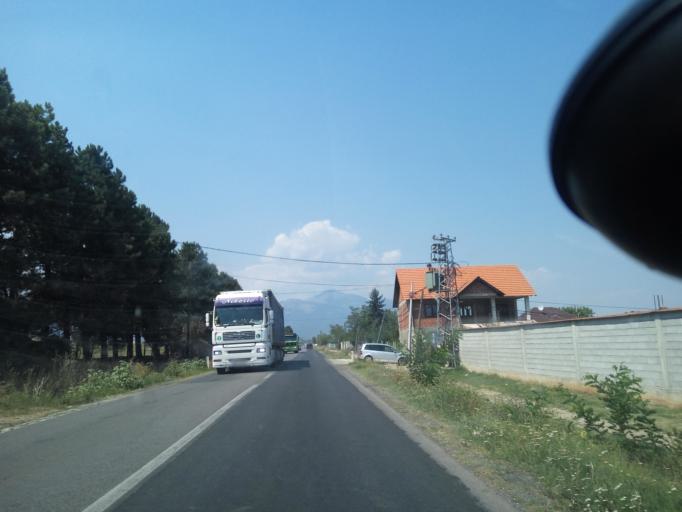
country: XK
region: Gjakova
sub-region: Komuna e Decanit
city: Gllogjan
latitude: 42.4715
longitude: 20.3424
